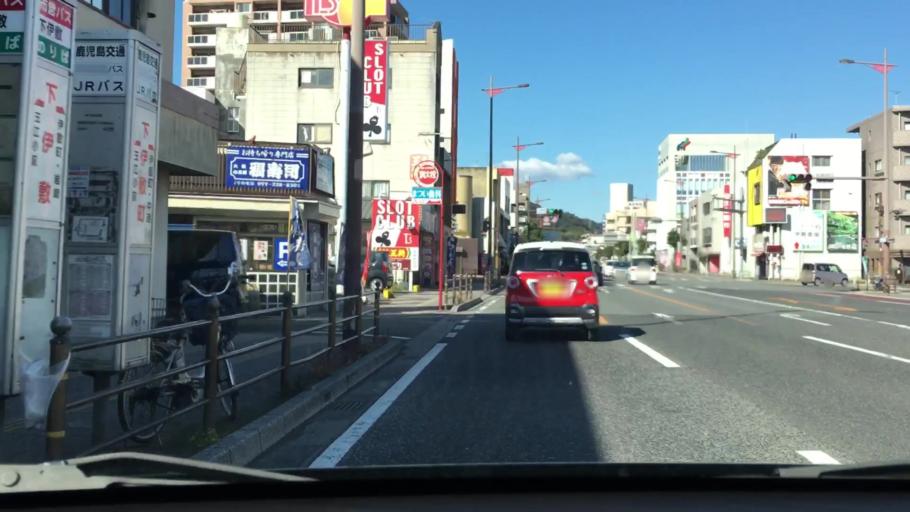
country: JP
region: Kagoshima
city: Kagoshima-shi
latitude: 31.6142
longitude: 130.5306
